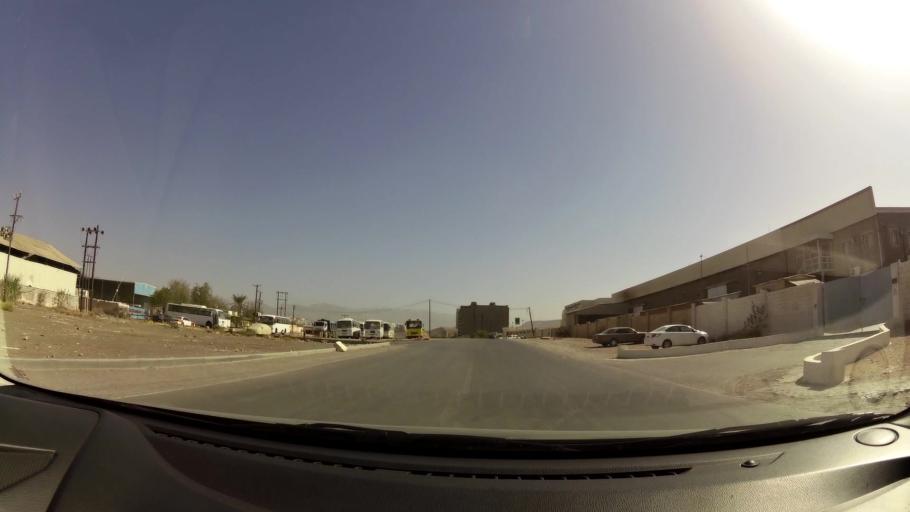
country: OM
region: Muhafazat Masqat
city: Bawshar
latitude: 23.5689
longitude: 58.3490
